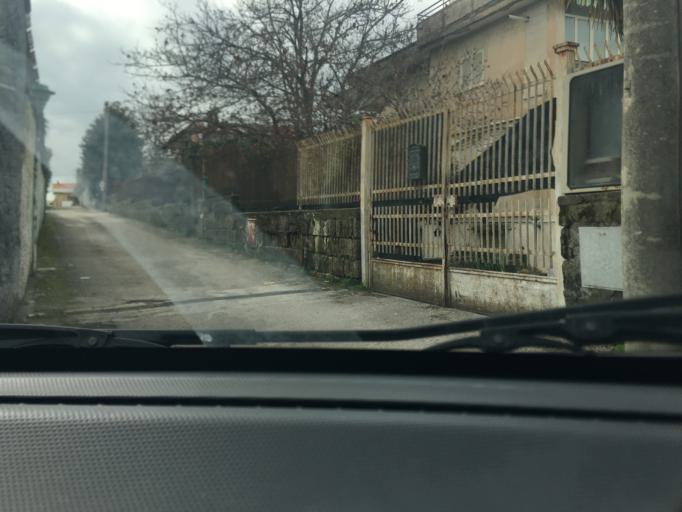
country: IT
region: Campania
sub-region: Provincia di Napoli
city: Marano di Napoli
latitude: 40.8914
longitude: 14.1778
